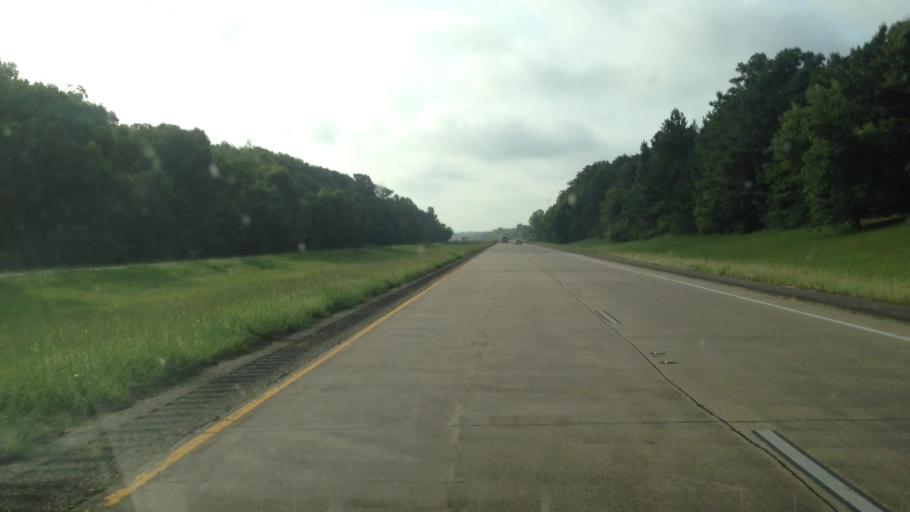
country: US
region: Louisiana
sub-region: Rapides Parish
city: Lecompte
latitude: 31.0229
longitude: -92.3950
